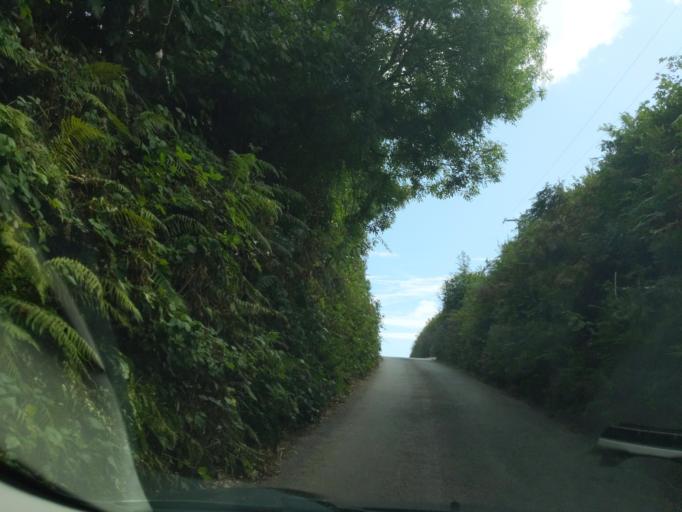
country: GB
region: England
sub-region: Devon
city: Modbury
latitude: 50.3567
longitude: -3.8887
